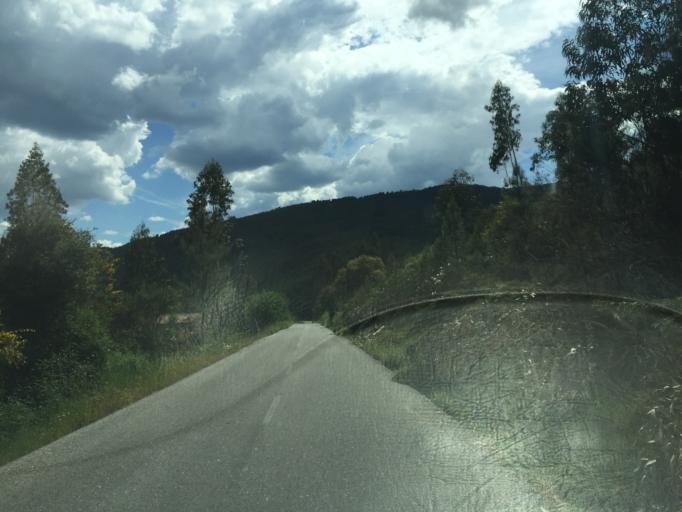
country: PT
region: Coimbra
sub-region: Pampilhosa da Serra
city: Pampilhosa da Serra
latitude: 40.0548
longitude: -7.8095
